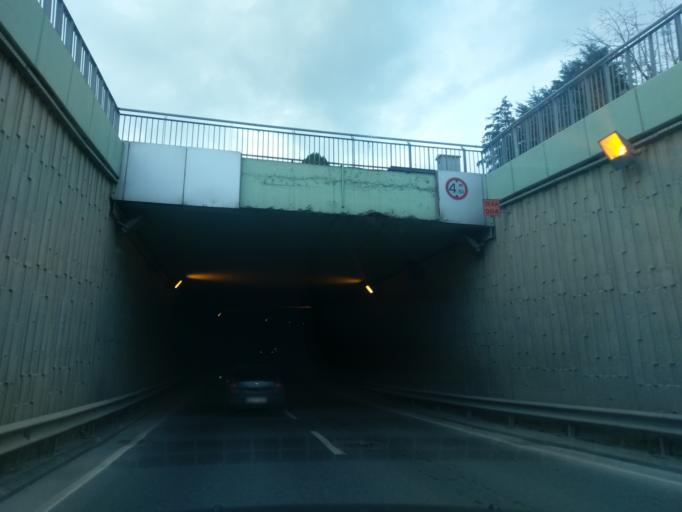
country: TR
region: Istanbul
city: Esenyurt
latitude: 41.0589
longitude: 28.6908
